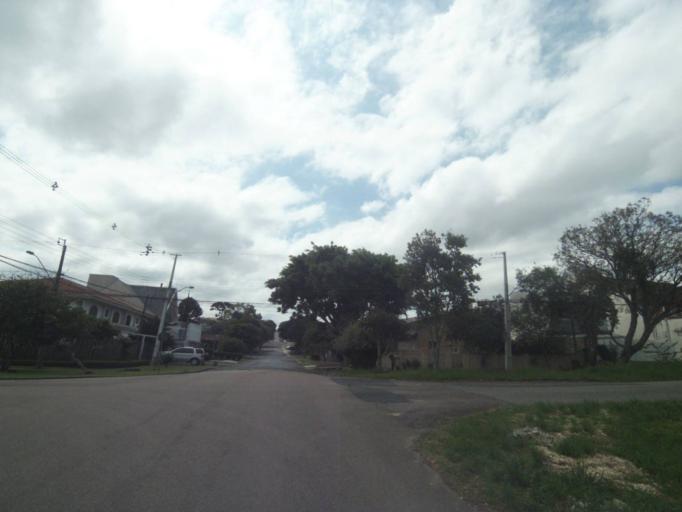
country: BR
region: Parana
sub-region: Pinhais
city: Pinhais
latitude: -25.4168
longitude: -49.2133
